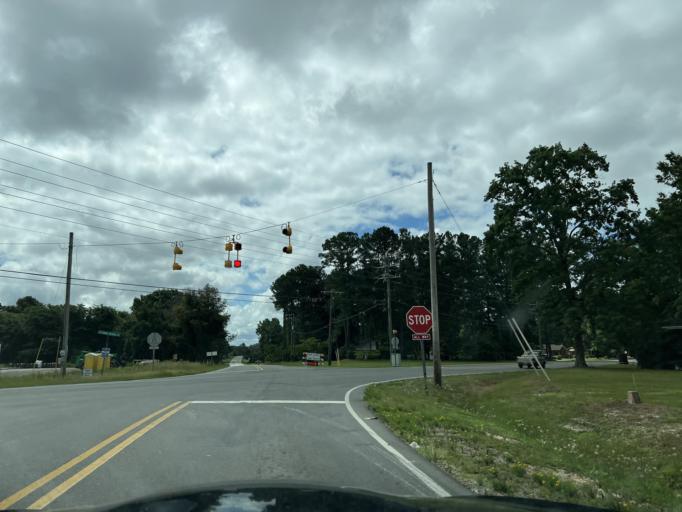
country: US
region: North Carolina
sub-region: Lee County
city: Sanford
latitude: 35.4352
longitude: -79.1666
